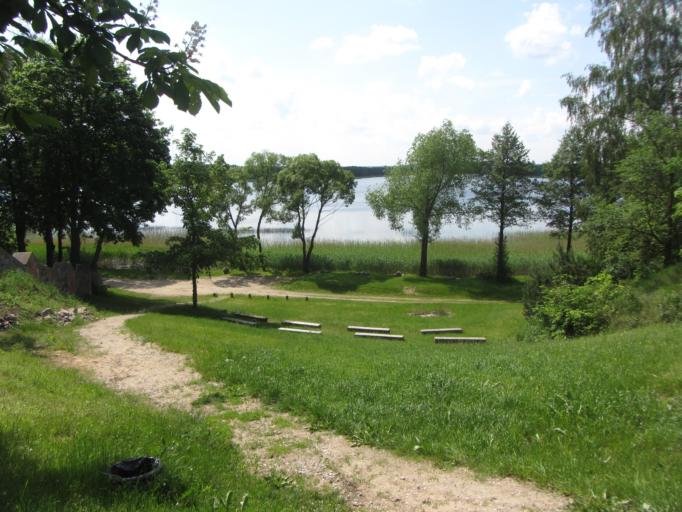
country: LT
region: Vilnius County
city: Elektrenai
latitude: 54.8620
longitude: 24.5918
